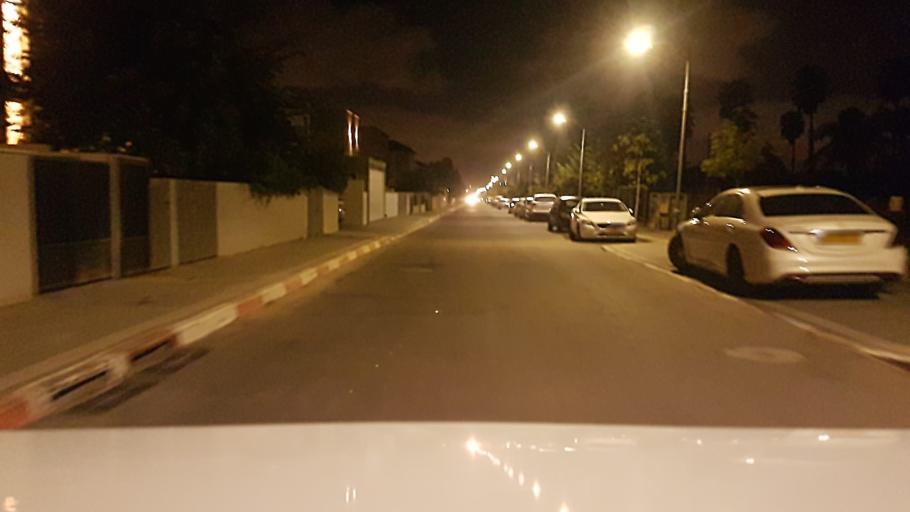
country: IL
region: Central District
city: Nehalim
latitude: 32.0735
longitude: 34.9269
